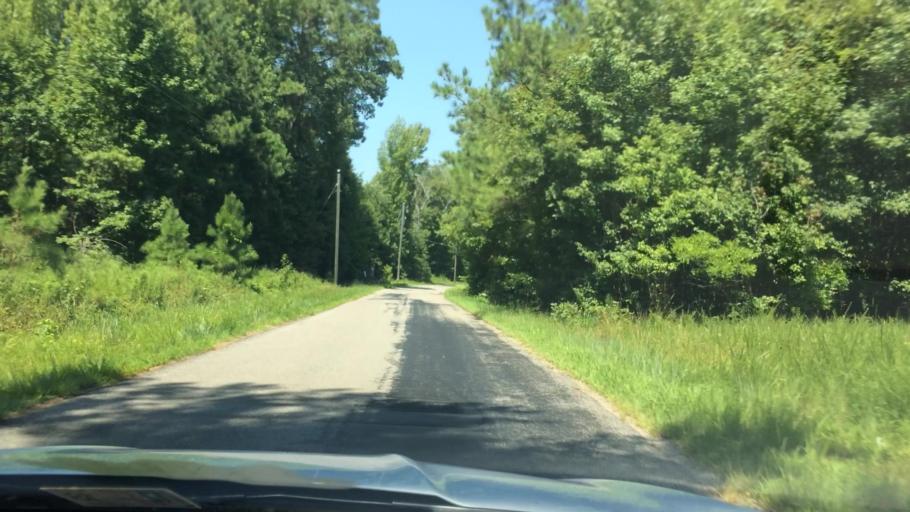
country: US
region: Virginia
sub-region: Charles City County
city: Charles City
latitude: 37.2860
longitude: -76.9318
